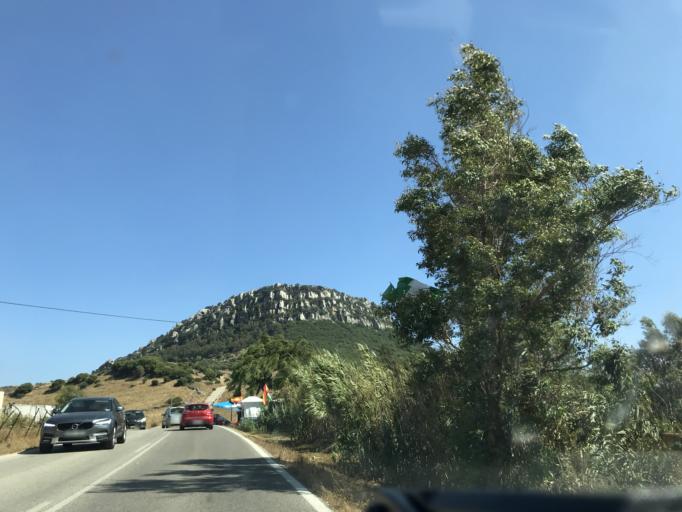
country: ES
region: Andalusia
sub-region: Provincia de Cadiz
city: Zahara de los Atunes
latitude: 36.1011
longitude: -5.7333
